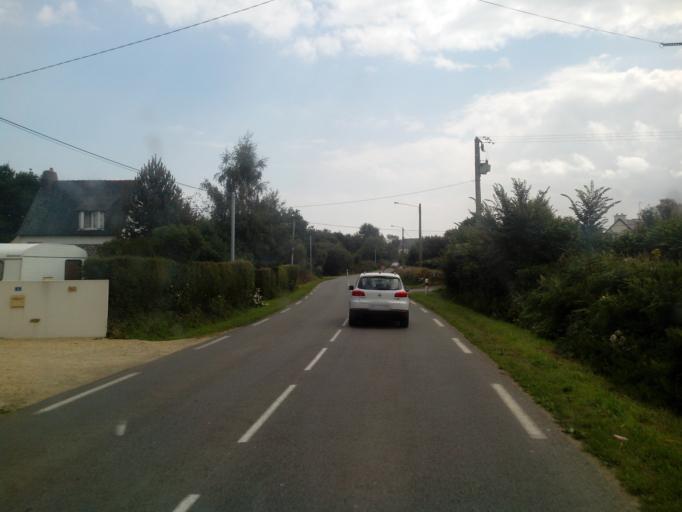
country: FR
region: Brittany
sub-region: Departement des Cotes-d'Armor
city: Plouha
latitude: 48.6994
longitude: -2.9432
